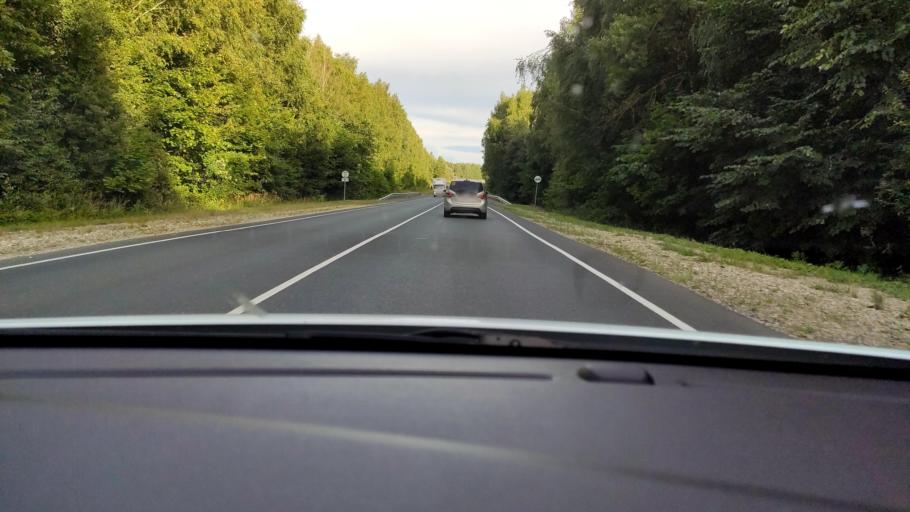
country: RU
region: Mariy-El
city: Krasnogorskiy
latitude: 56.1833
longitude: 48.2589
